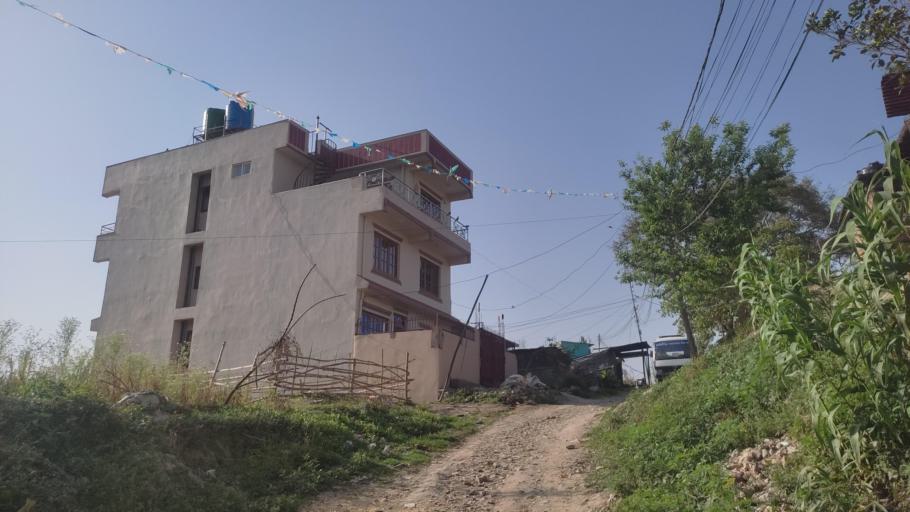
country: NP
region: Central Region
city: Kirtipur
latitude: 27.6593
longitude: 85.2791
